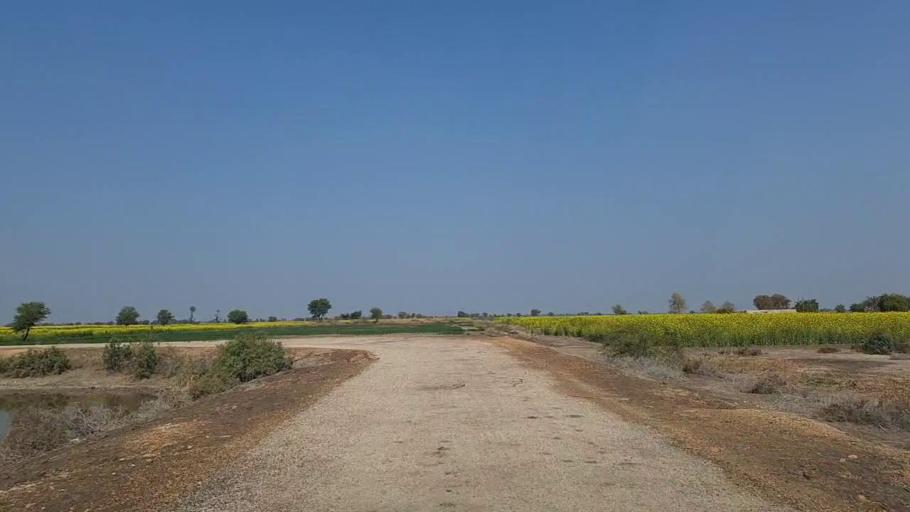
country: PK
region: Sindh
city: Nawabshah
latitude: 26.2943
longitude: 68.4810
